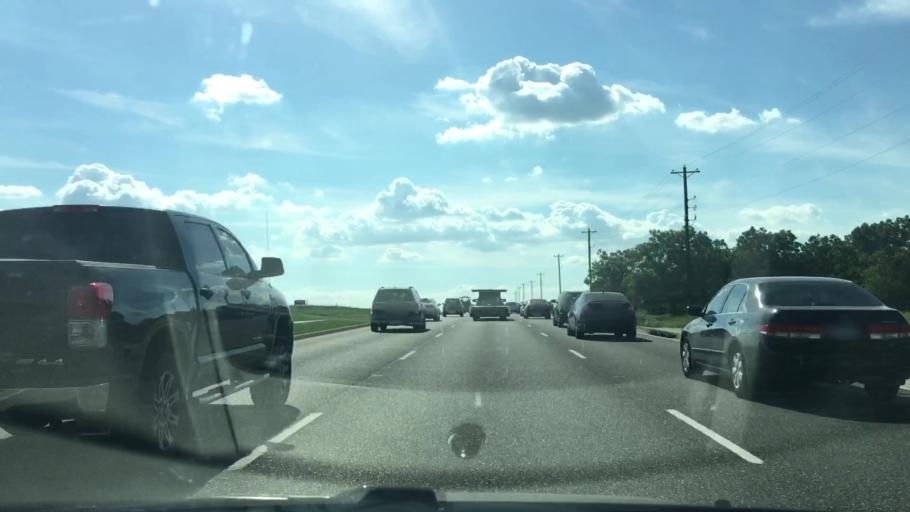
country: US
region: Texas
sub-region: Collin County
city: Prosper
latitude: 33.2190
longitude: -96.7249
